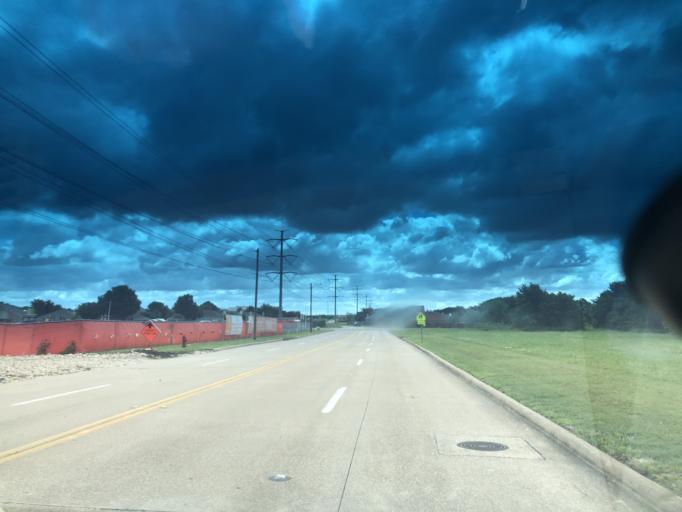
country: US
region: Texas
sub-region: Dallas County
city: Grand Prairie
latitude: 32.6980
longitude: -97.0344
